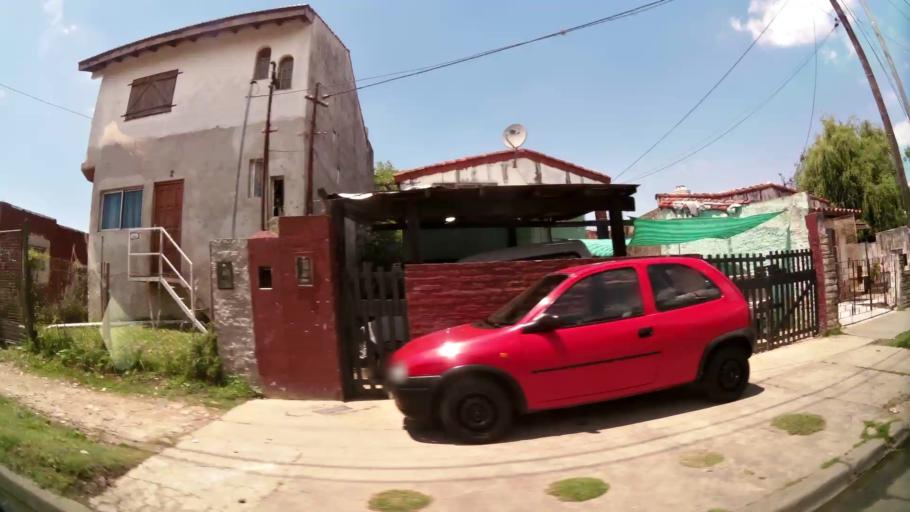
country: AR
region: Buenos Aires
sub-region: Partido de Tigre
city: Tigre
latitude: -34.4134
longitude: -58.6004
